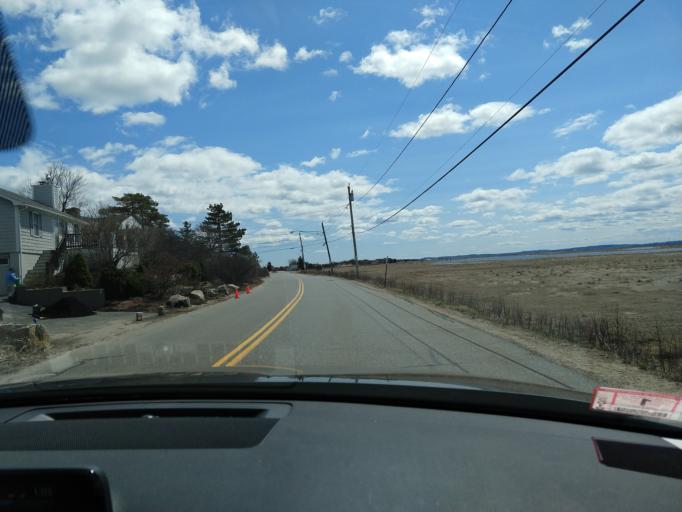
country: US
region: Massachusetts
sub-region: Essex County
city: Newburyport
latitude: 42.7930
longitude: -70.8113
